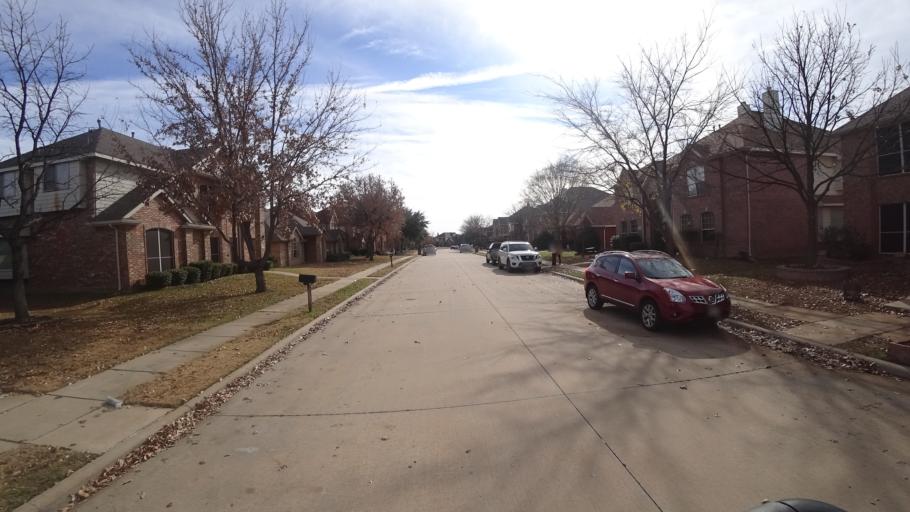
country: US
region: Texas
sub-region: Denton County
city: Highland Village
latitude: 33.0651
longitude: -97.0317
